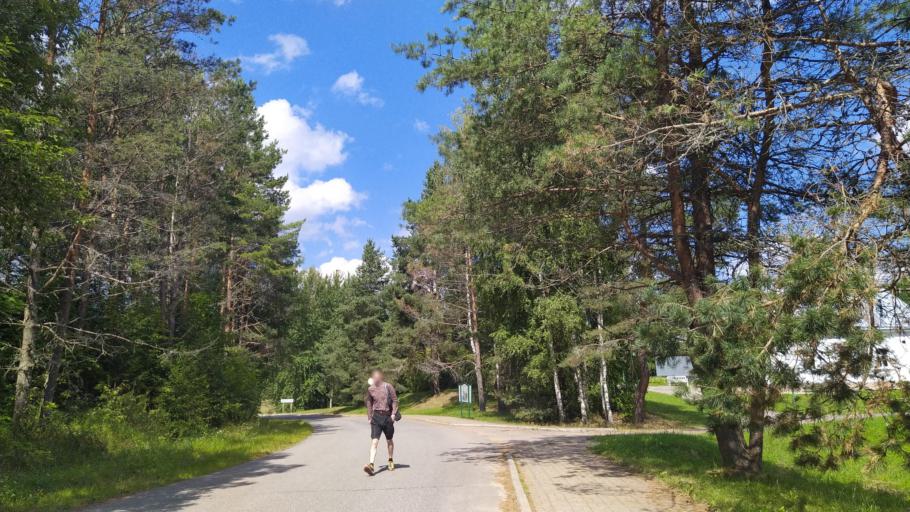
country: RU
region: Pskov
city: Pushkinskiye Gory
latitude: 57.0756
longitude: 28.9562
